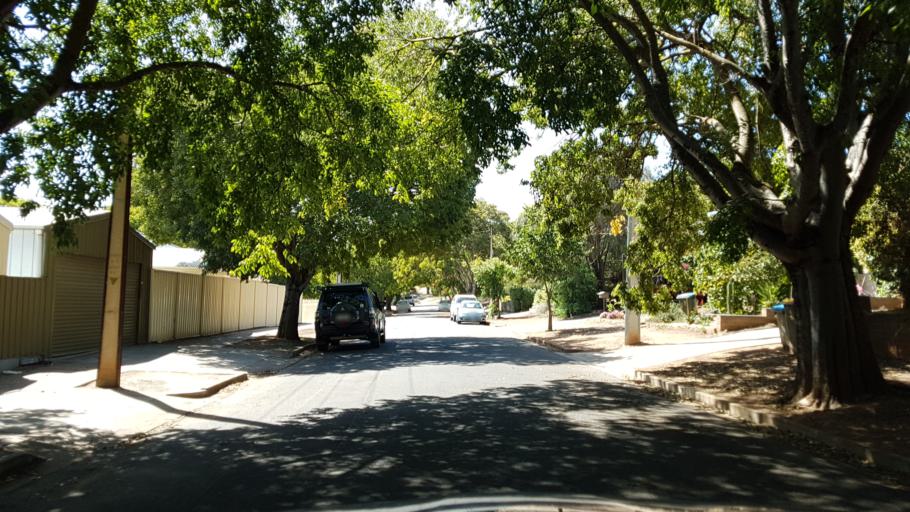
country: AU
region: South Australia
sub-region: Onkaparinga
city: Bedford Park
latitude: -35.0278
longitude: 138.5649
